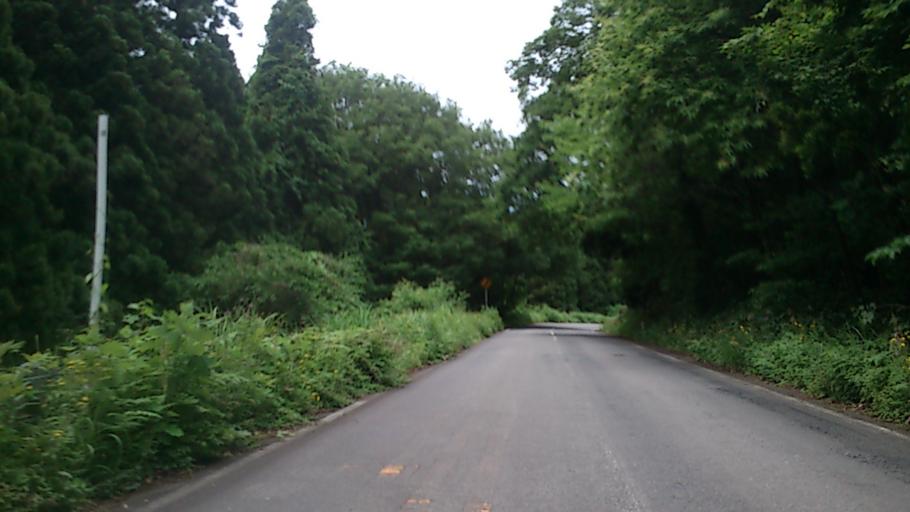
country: JP
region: Yamagata
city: Yuza
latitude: 39.0928
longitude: 139.9108
